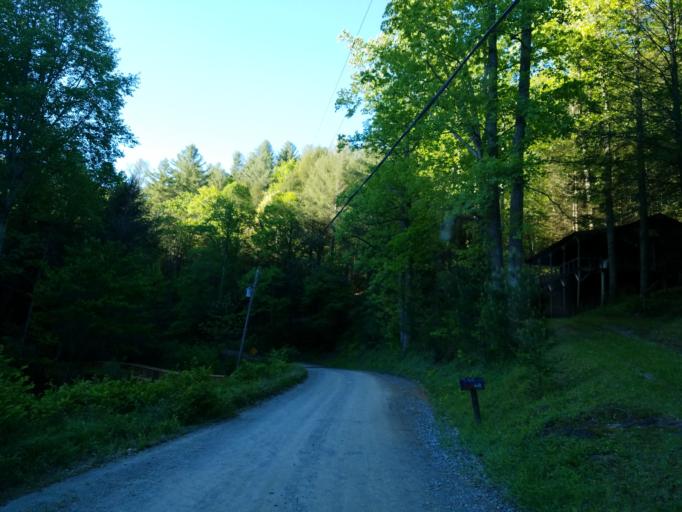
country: US
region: Georgia
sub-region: Fannin County
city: Blue Ridge
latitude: 34.7406
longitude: -84.2903
